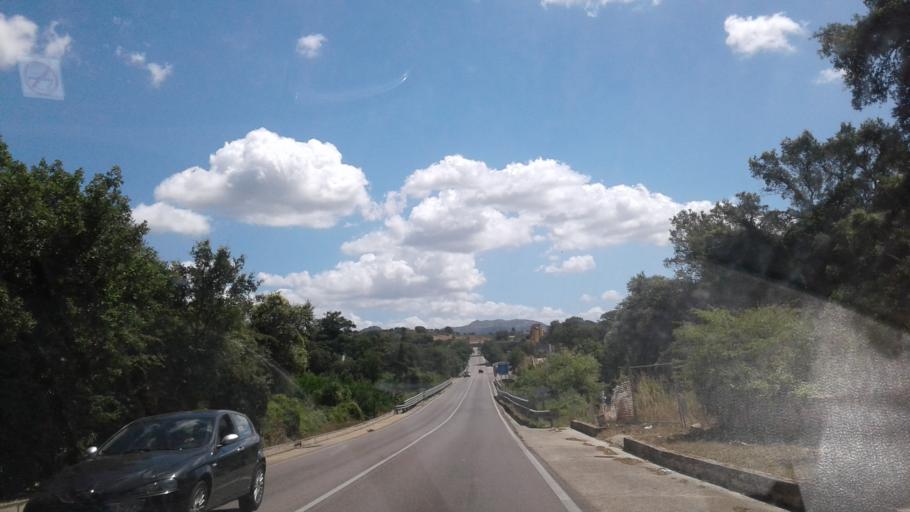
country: IT
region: Sardinia
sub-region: Provincia di Olbia-Tempio
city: Tempio Pausania
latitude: 40.9063
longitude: 9.1400
